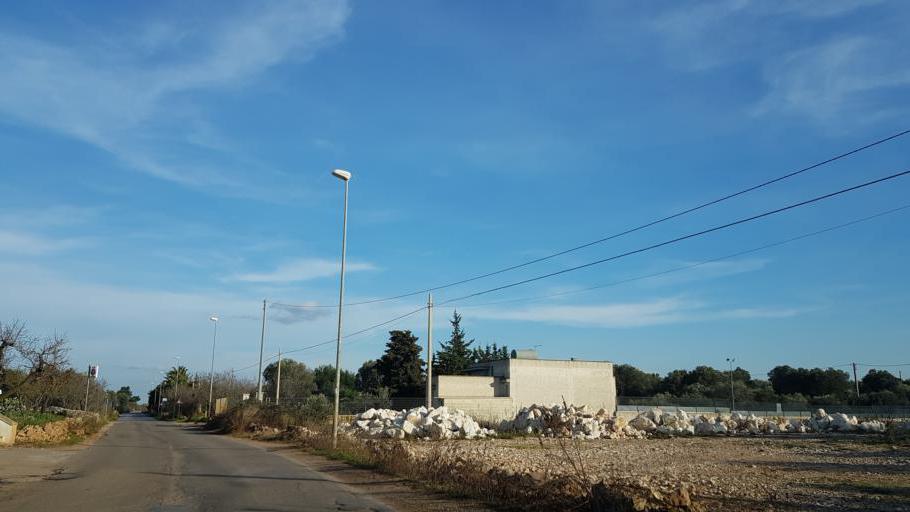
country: IT
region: Apulia
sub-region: Provincia di Brindisi
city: Carovigno
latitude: 40.7010
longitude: 17.6730
